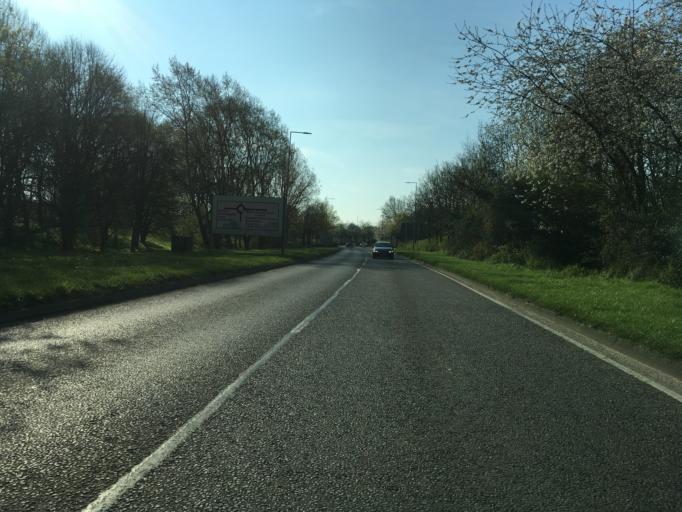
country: GB
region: England
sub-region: Milton Keynes
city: Newport Pagnell
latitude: 52.0683
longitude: -0.7412
